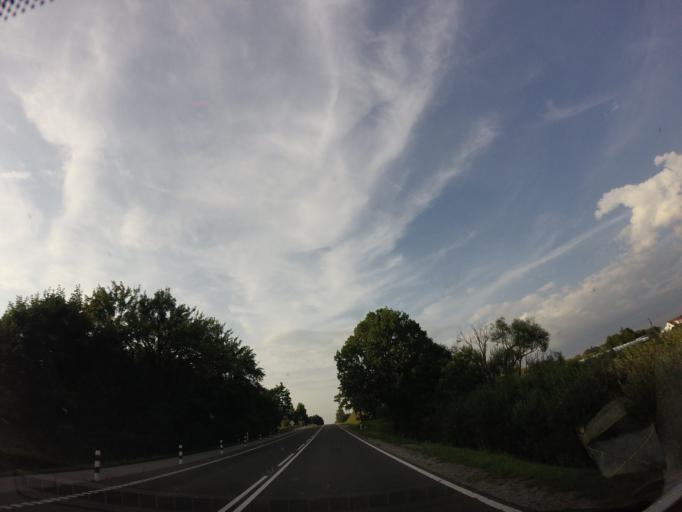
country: LT
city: Lazdijai
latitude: 54.1509
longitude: 23.4701
